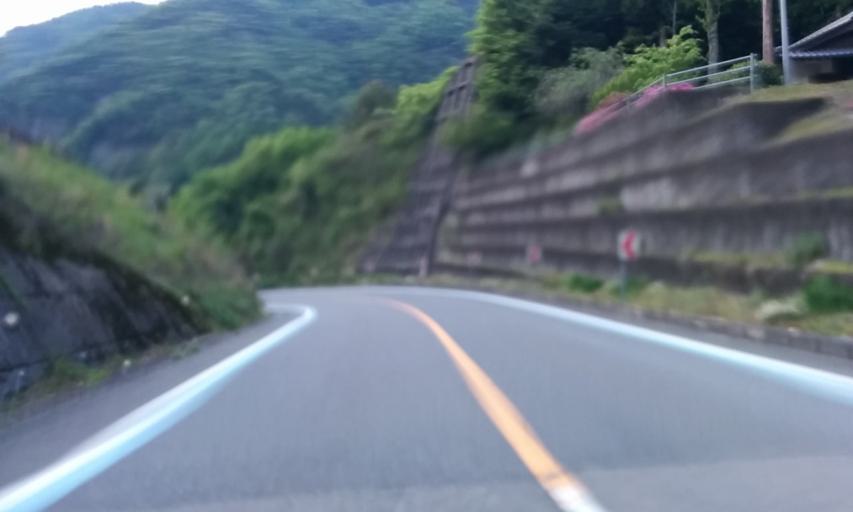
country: JP
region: Ehime
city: Saijo
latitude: 33.8482
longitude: 133.2153
